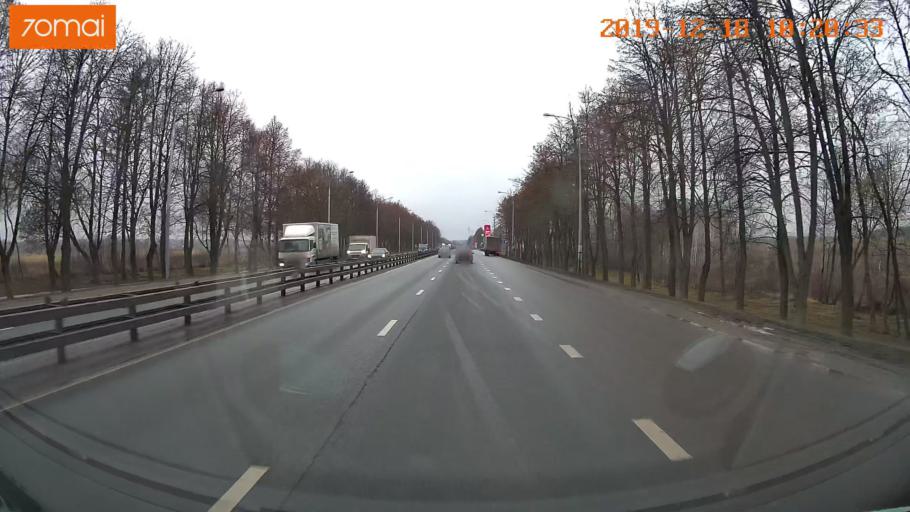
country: RU
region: Moskovskaya
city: Dubrovitsy
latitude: 55.3929
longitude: 37.4302
